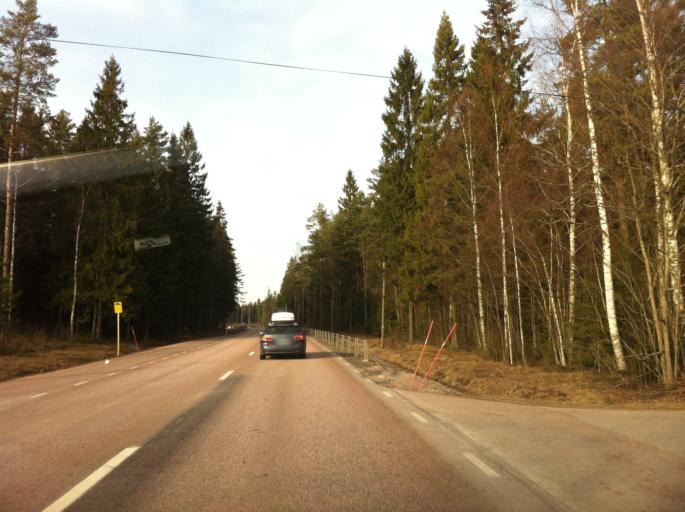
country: SE
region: Vaermland
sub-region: Kristinehamns Kommun
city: Bjorneborg
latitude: 59.2491
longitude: 14.1775
